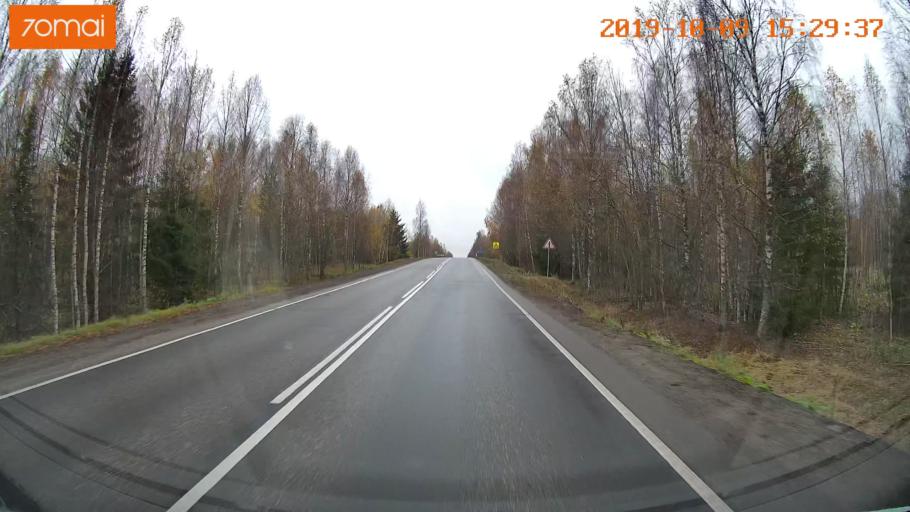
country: RU
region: Kostroma
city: Susanino
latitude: 57.9892
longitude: 41.3396
